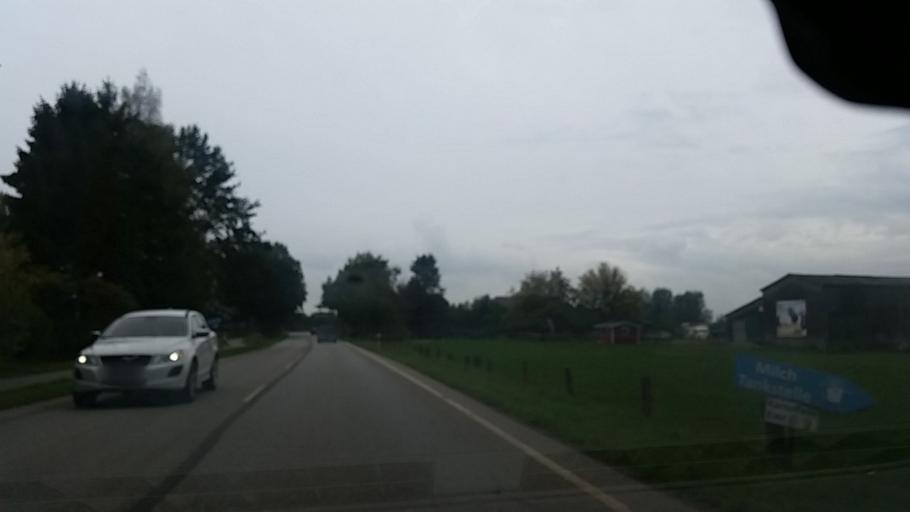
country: DE
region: Schleswig-Holstein
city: Nahe
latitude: 53.7843
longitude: 10.1309
